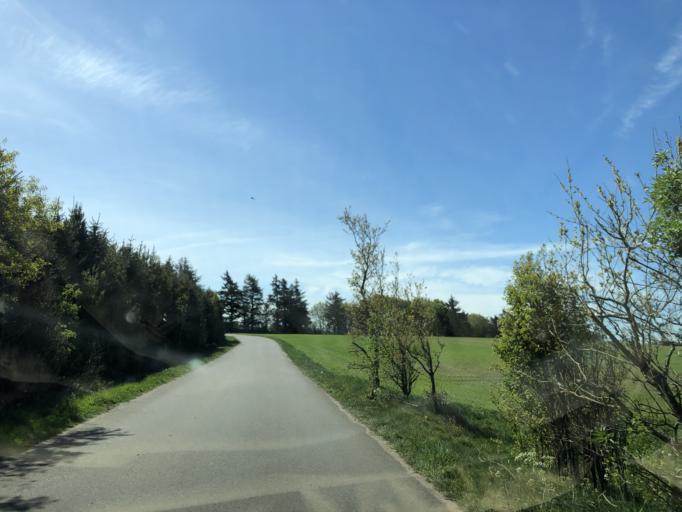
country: DK
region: Central Jutland
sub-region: Ringkobing-Skjern Kommune
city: Videbaek
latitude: 56.1941
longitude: 8.5114
